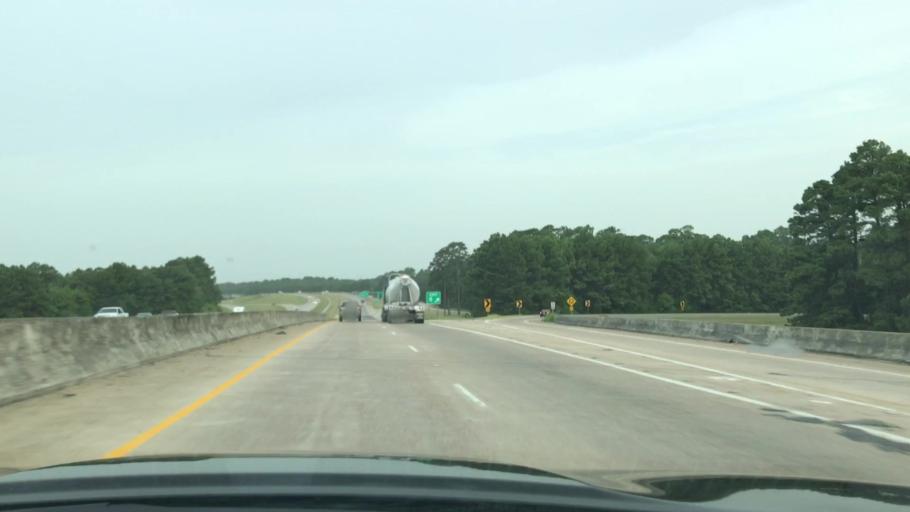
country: US
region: Louisiana
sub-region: Bossier Parish
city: Bossier City
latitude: 32.4158
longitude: -93.7889
